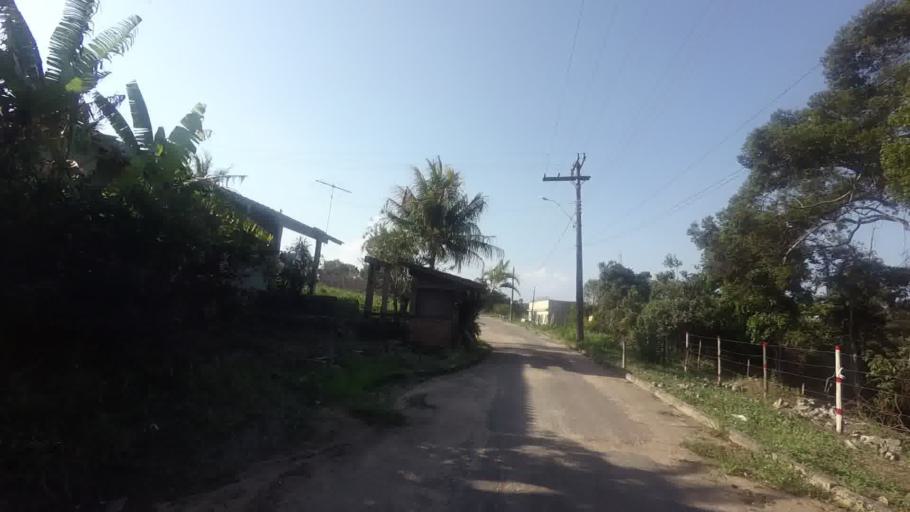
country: BR
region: Espirito Santo
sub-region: Guarapari
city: Guarapari
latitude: -20.7272
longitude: -40.5363
